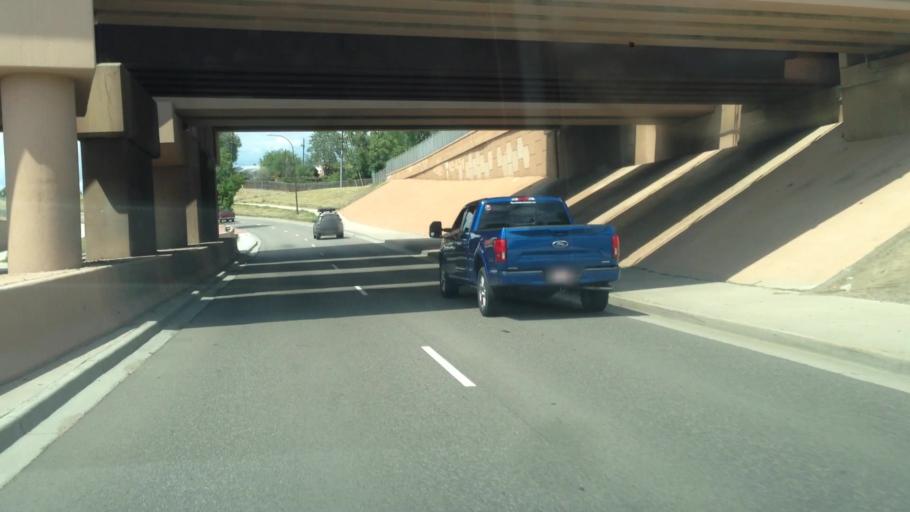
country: US
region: Colorado
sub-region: Jefferson County
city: Arvada
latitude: 39.7927
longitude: -105.1093
